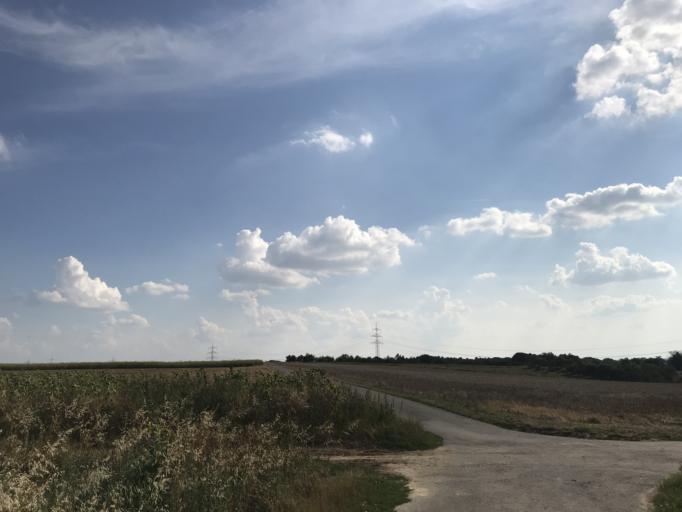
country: DE
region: Hesse
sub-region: Regierungsbezirk Darmstadt
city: Wolfersheim
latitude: 50.3515
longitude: 8.8140
